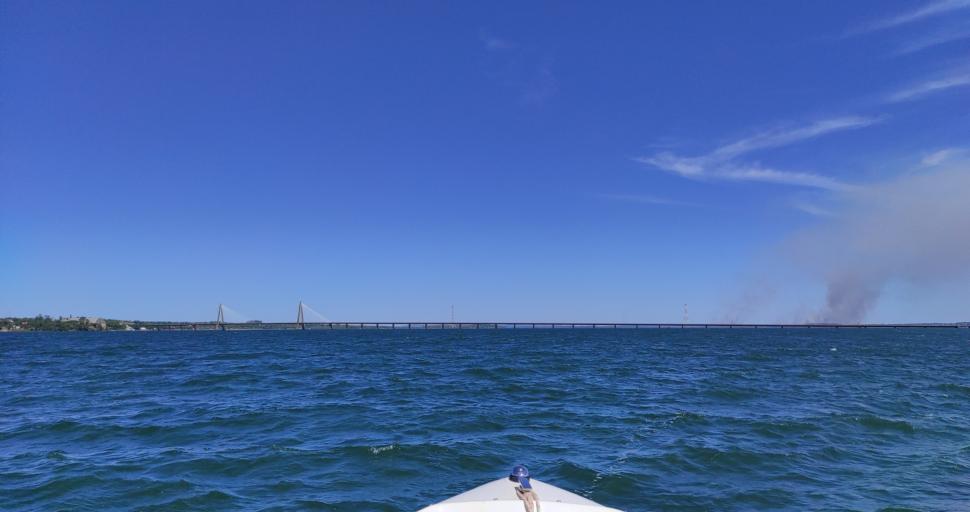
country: AR
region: Misiones
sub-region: Departamento de Capital
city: Posadas
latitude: -27.3606
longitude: -55.8845
